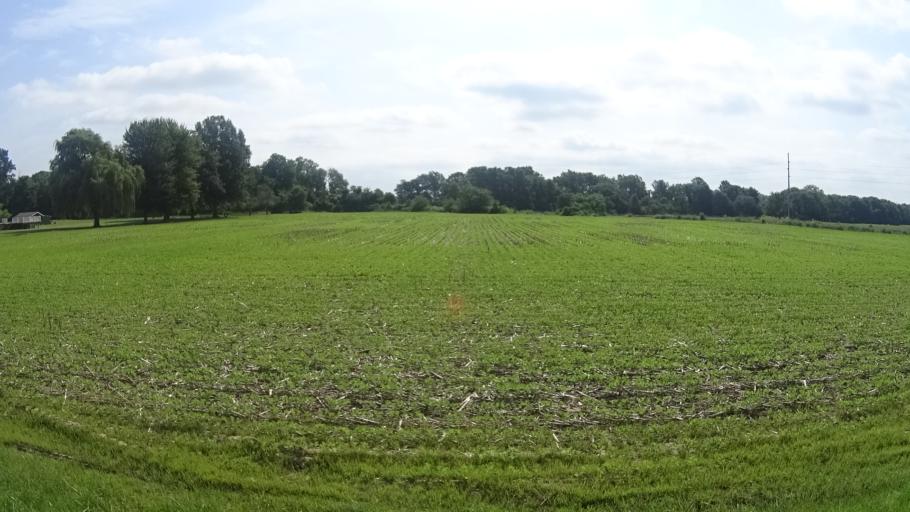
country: US
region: Ohio
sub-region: Lorain County
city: Vermilion
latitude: 41.3886
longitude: -82.4188
